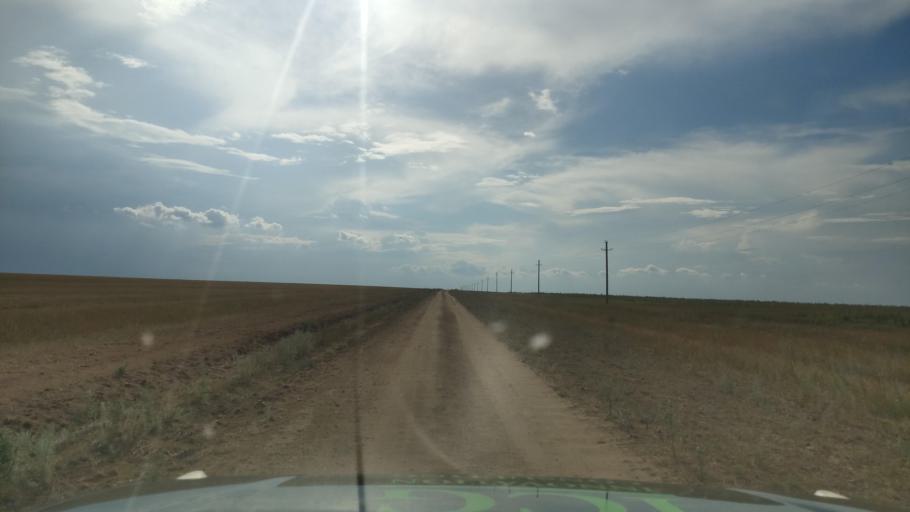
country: KZ
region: Pavlodar
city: Pavlodar
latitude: 52.5092
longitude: 77.5763
